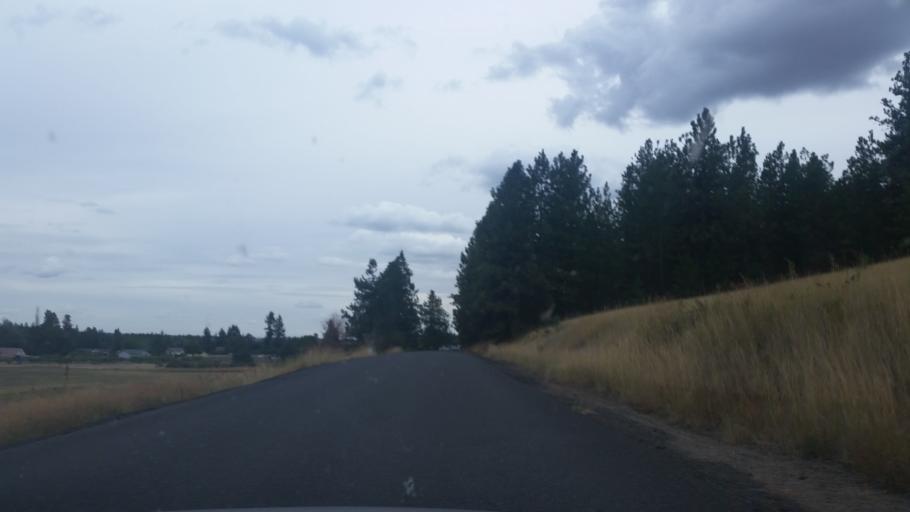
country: US
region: Washington
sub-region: Spokane County
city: Cheney
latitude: 47.5171
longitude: -117.5744
